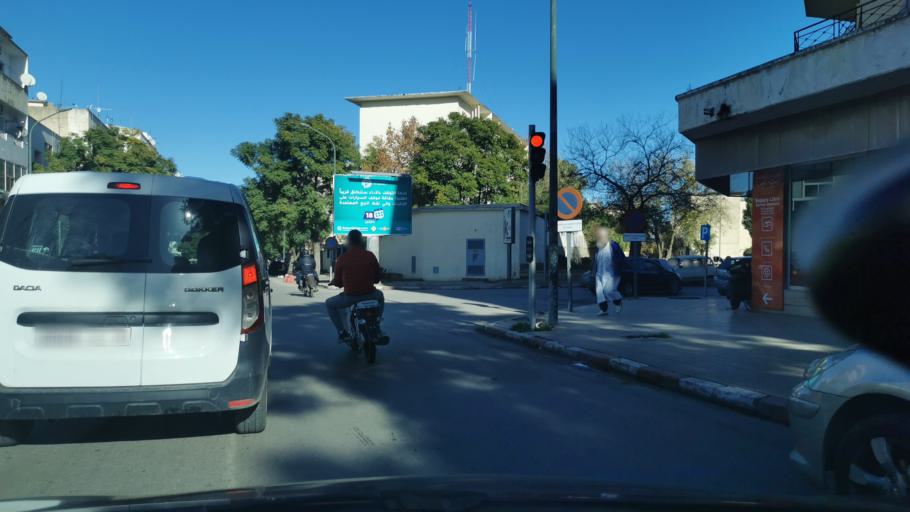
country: MA
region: Fes-Boulemane
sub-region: Fes
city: Fes
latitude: 34.0402
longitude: -5.0058
